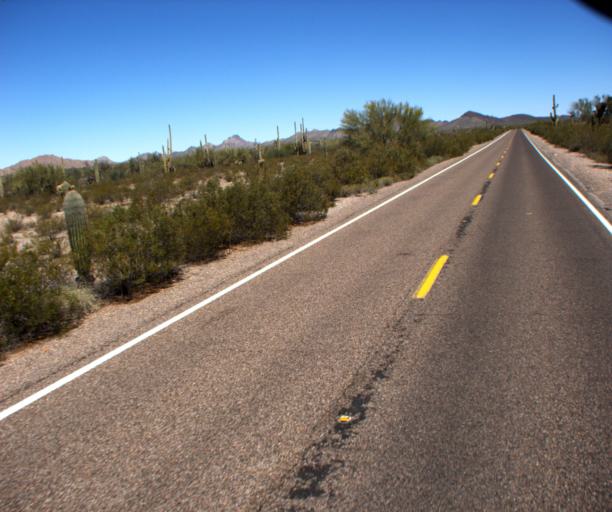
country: MX
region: Sonora
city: Sonoyta
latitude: 31.9012
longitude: -112.8114
